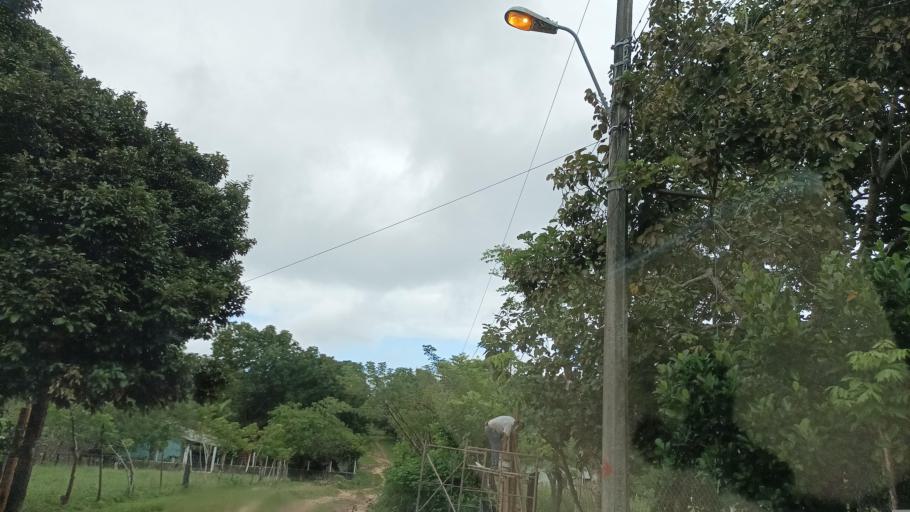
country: MX
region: Veracruz
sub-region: Cosoleacaque
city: Residencial las Olas
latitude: 18.0720
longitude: -94.5852
